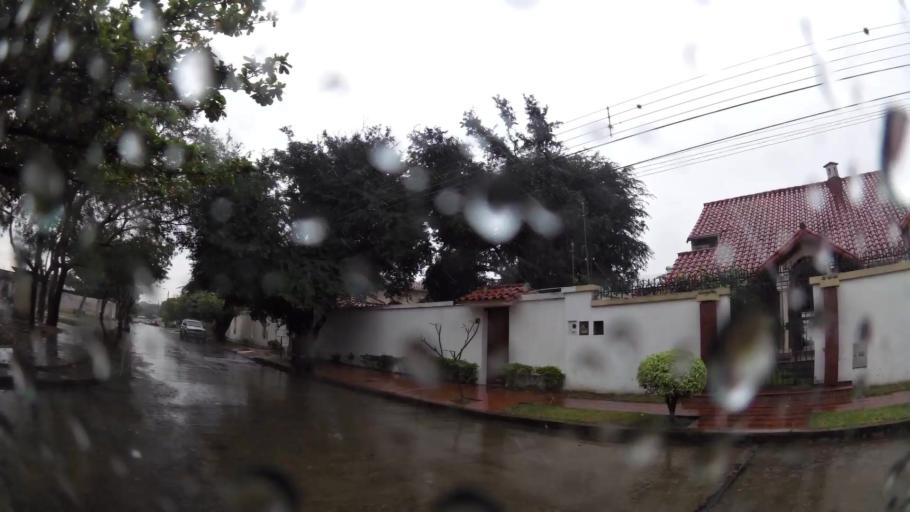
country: BO
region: Santa Cruz
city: Santa Cruz de la Sierra
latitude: -17.8019
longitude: -63.1631
